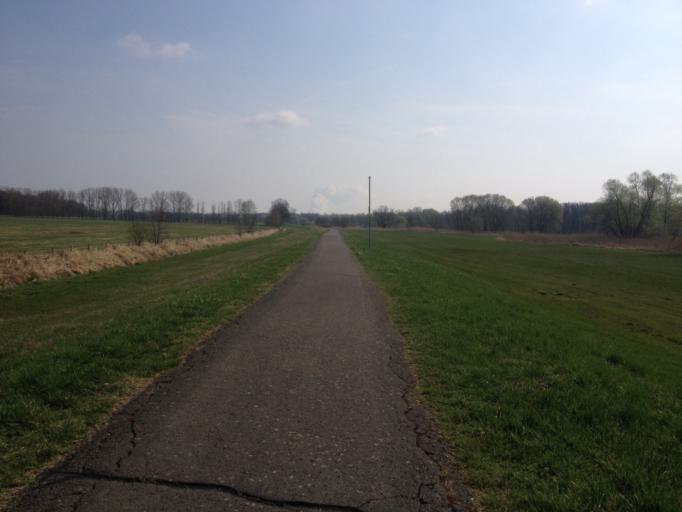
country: DE
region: Brandenburg
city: Briesen
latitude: 51.8459
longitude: 14.2748
